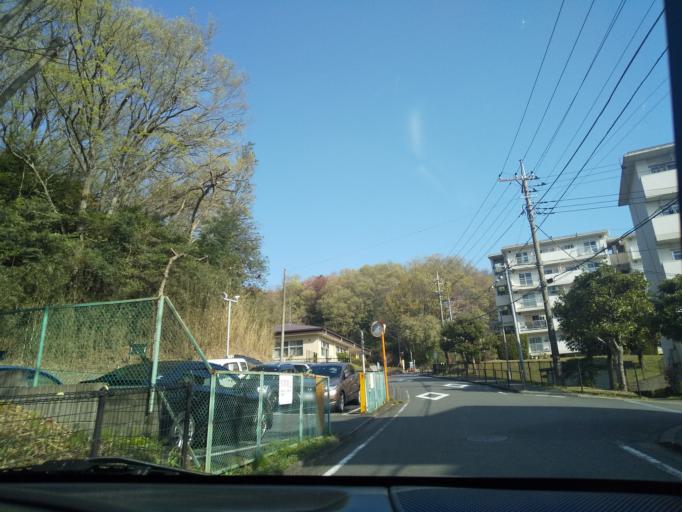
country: JP
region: Tokyo
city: Hino
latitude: 35.6457
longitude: 139.4165
